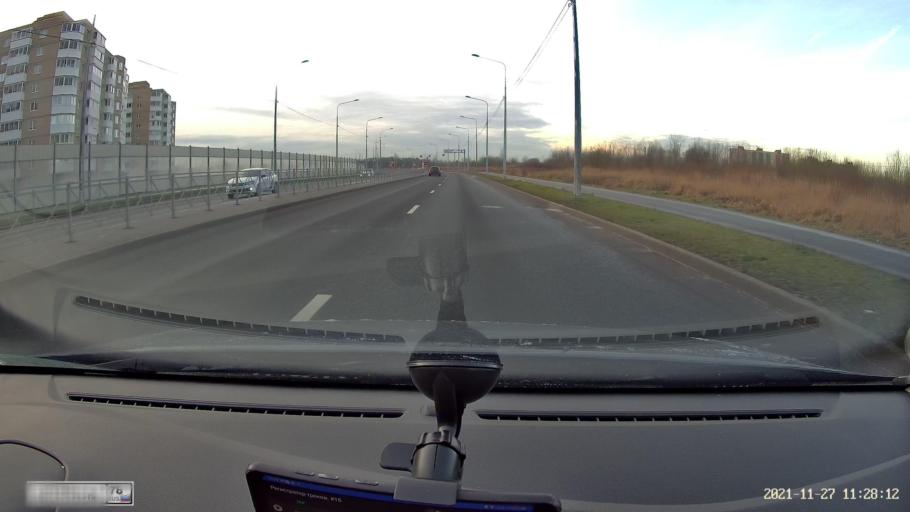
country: RU
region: St.-Petersburg
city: Krasnoye Selo
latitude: 59.7463
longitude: 30.0769
